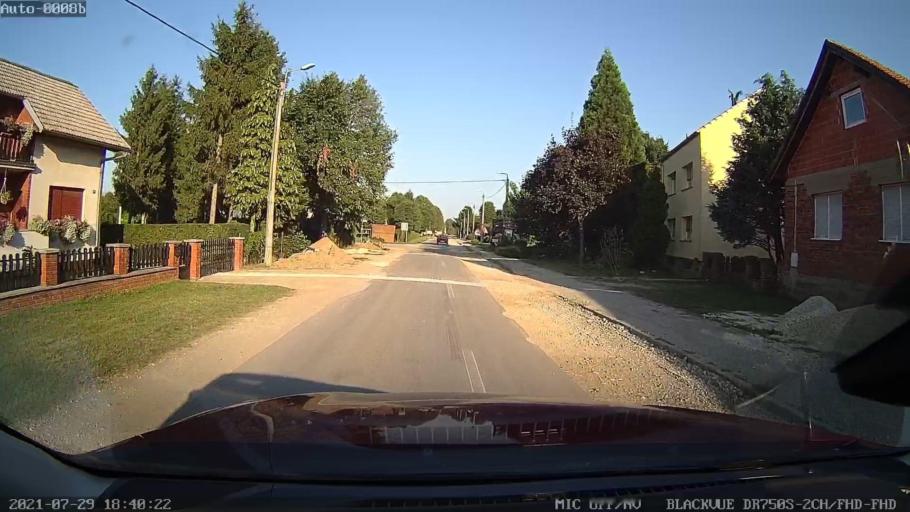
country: HR
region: Varazdinska
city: Petrijanec
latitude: 46.3199
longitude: 16.2289
